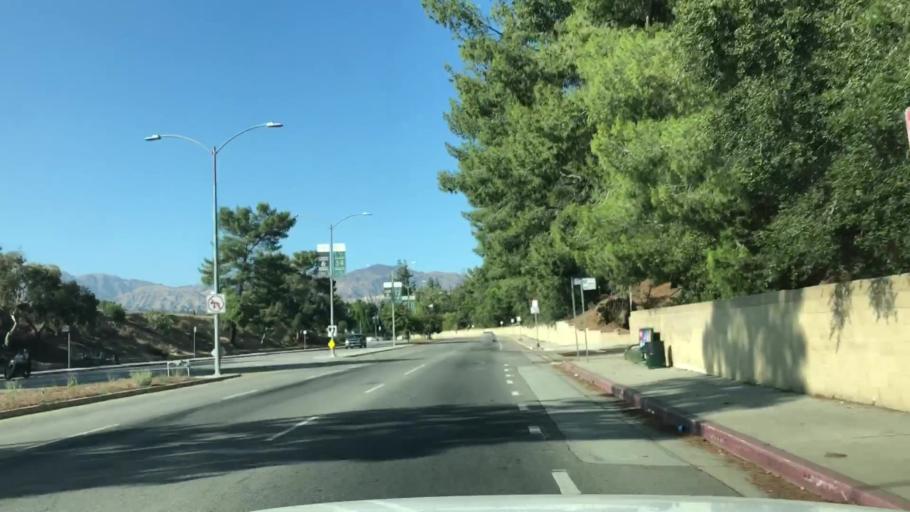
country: US
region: California
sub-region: Los Angeles County
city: Northridge
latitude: 34.2635
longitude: -118.5563
